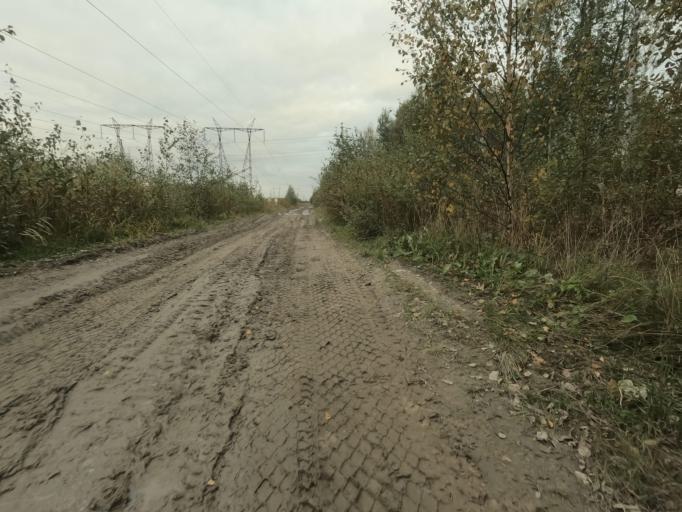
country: RU
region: St.-Petersburg
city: Sapernyy
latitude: 59.7540
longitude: 30.6992
